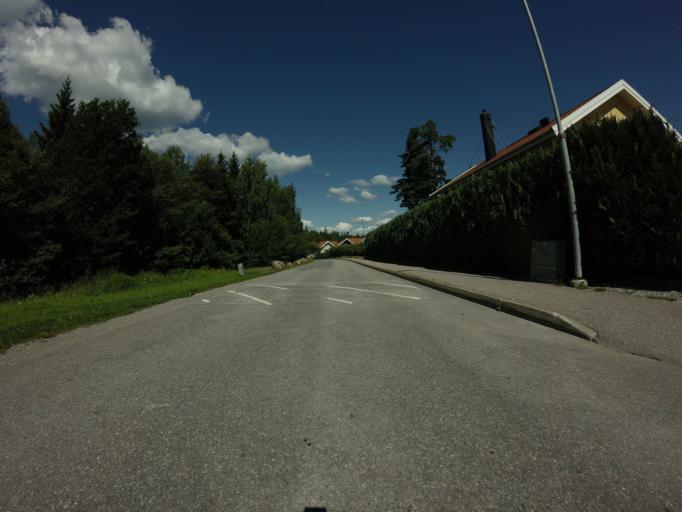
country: SE
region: Stockholm
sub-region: Jarfalla Kommun
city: Jakobsberg
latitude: 59.4573
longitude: 17.8874
